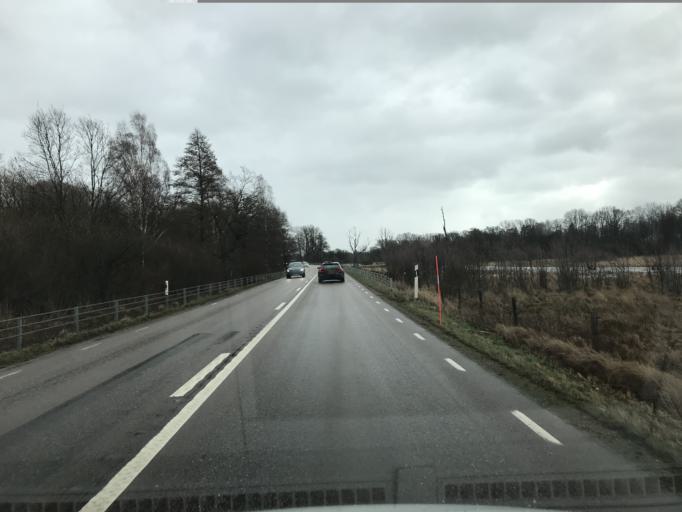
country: SE
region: Skane
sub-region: Klippans Kommun
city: Ljungbyhed
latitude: 56.0894
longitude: 13.2256
